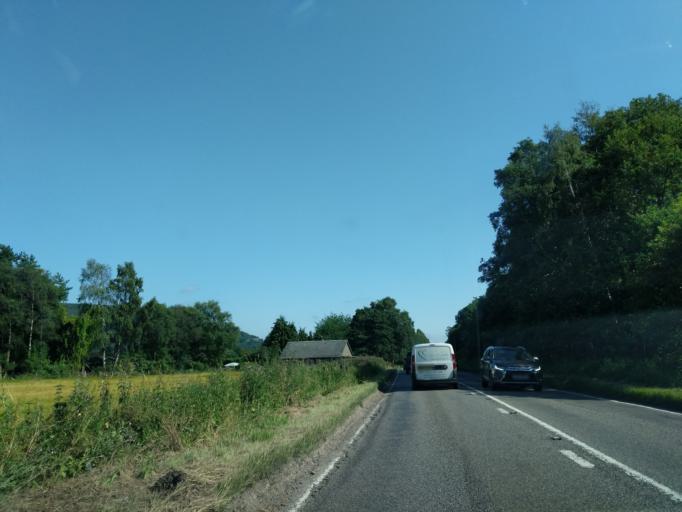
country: GB
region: Scotland
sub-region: Moray
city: Rothes
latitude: 57.5092
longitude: -3.2025
